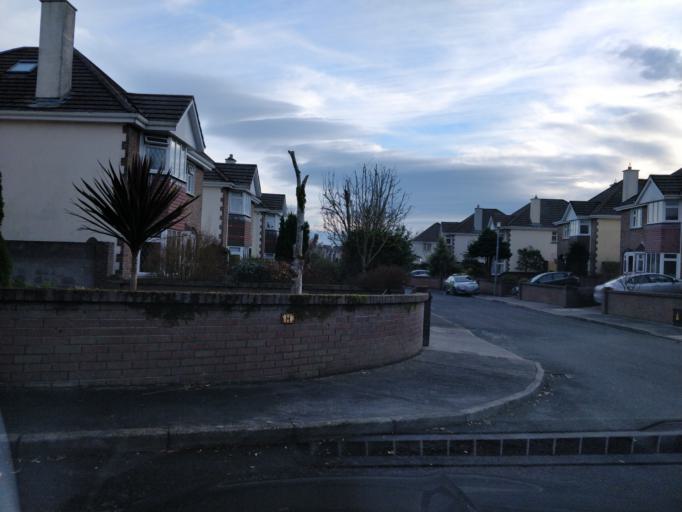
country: IE
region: Connaught
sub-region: County Galway
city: Bearna
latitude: 53.2674
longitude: -9.1088
